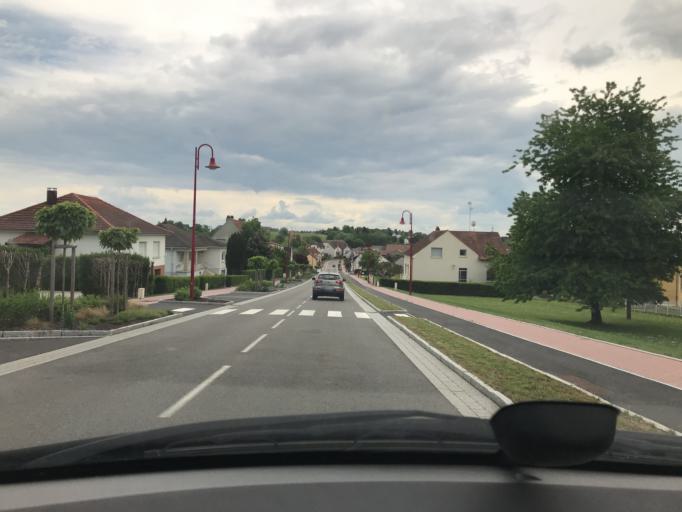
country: FR
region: Lorraine
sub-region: Departement de la Moselle
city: Neufgrange
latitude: 49.0838
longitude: 7.0403
